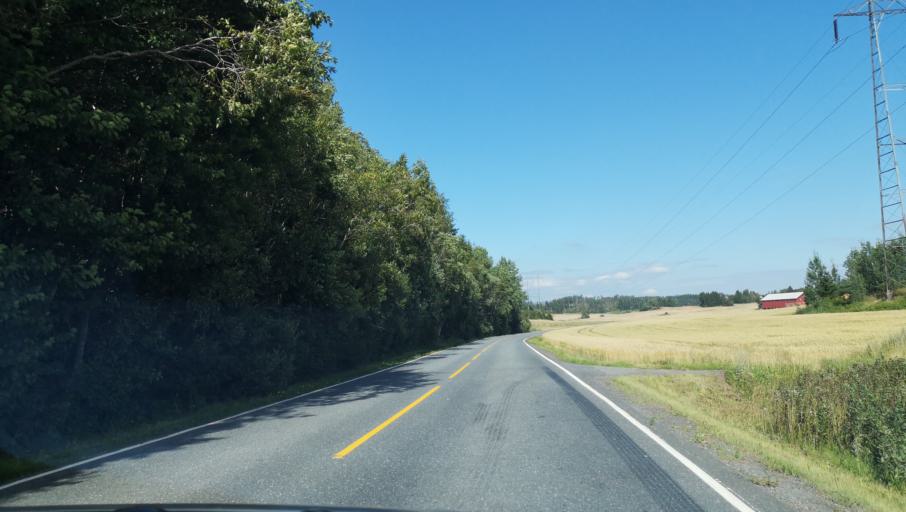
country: NO
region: Akershus
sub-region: Vestby
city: Vestby
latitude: 59.5411
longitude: 10.7765
